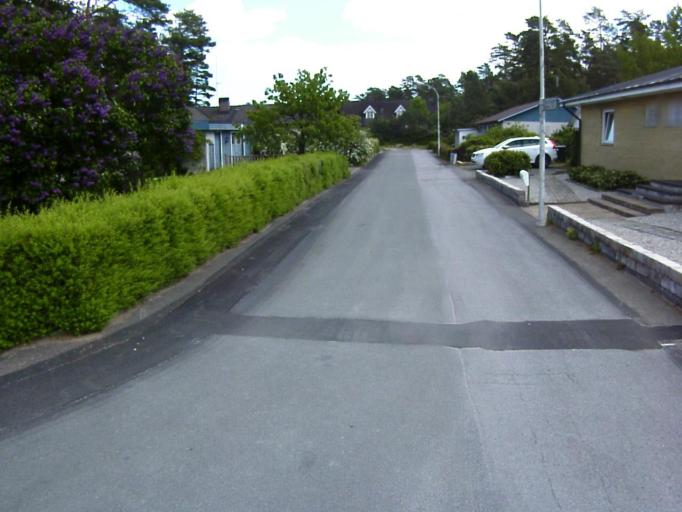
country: SE
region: Skane
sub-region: Kristianstads Kommun
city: Ahus
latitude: 55.9438
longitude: 14.2766
